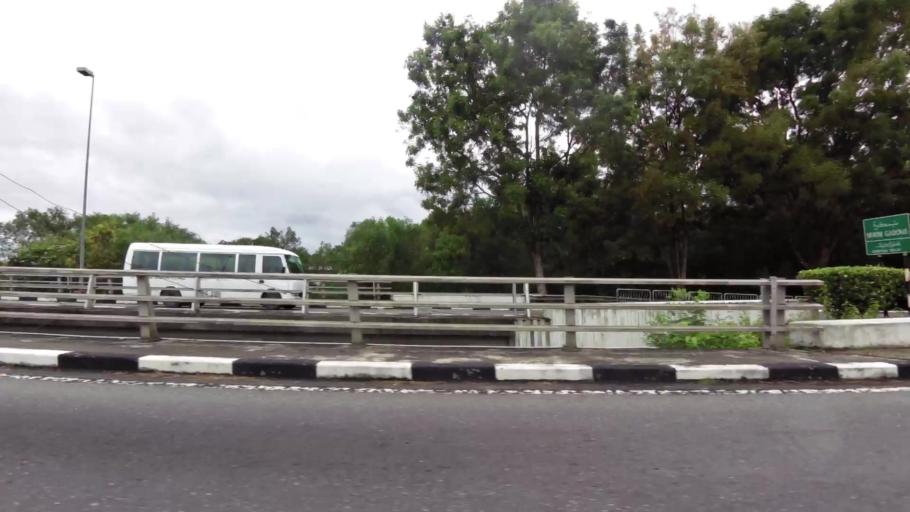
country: BN
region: Brunei and Muara
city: Bandar Seri Begawan
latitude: 4.8979
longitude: 114.9332
